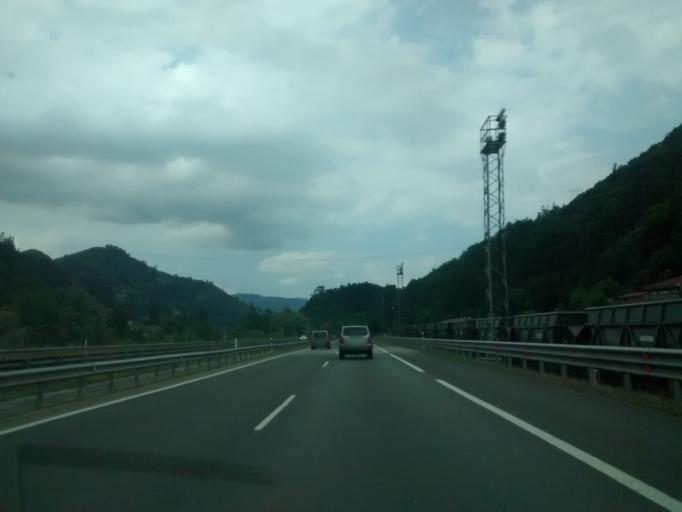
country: ES
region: Asturias
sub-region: Province of Asturias
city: Mieres
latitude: 43.2144
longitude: -5.7843
